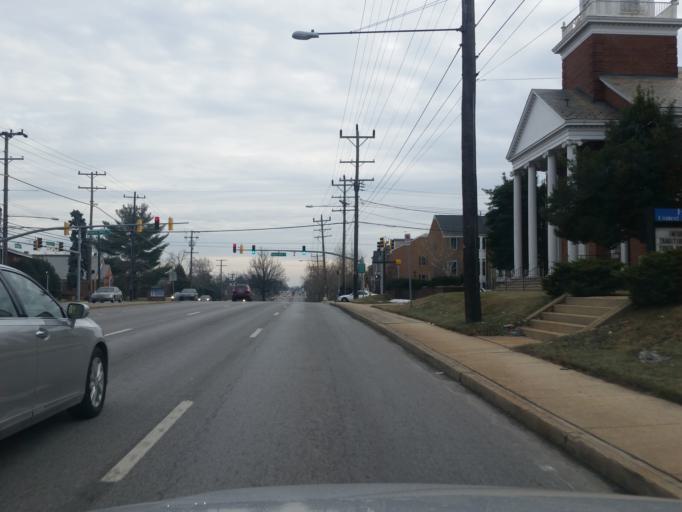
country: US
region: Maryland
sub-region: Montgomery County
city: Wheaton
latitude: 39.0307
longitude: -77.0480
